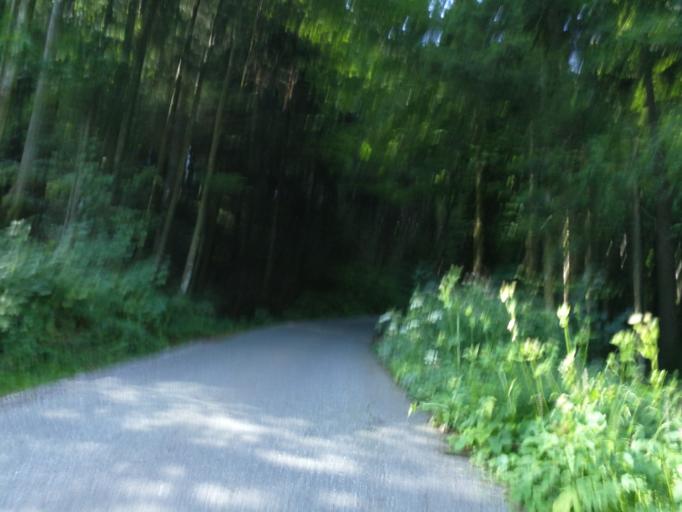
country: CH
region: Saint Gallen
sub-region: Wahlkreis See-Gaster
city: Gommiswald
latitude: 47.2508
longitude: 9.0447
